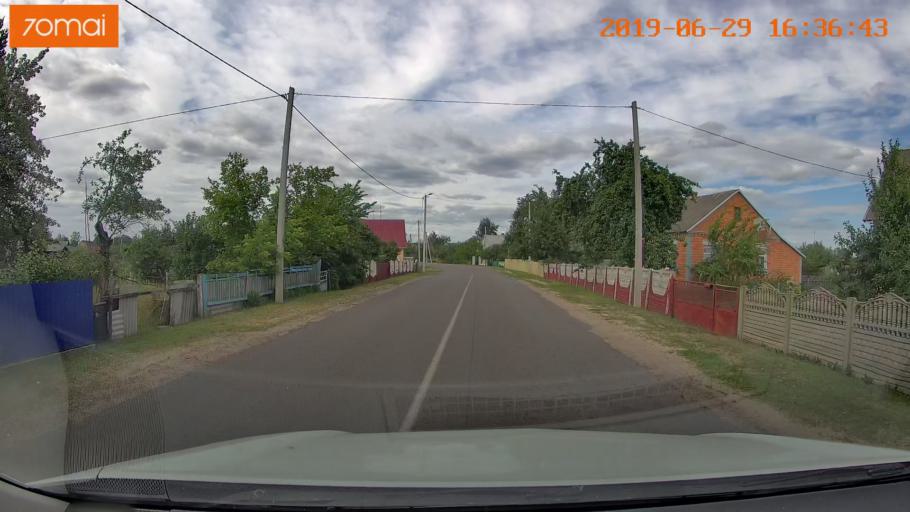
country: BY
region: Brest
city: Luninyets
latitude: 52.2216
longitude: 27.0250
